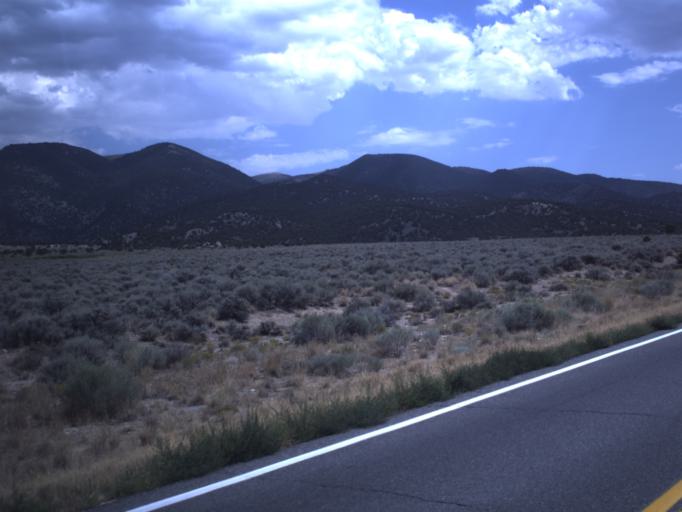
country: US
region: Utah
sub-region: Tooele County
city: Tooele
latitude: 40.3541
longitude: -112.3133
